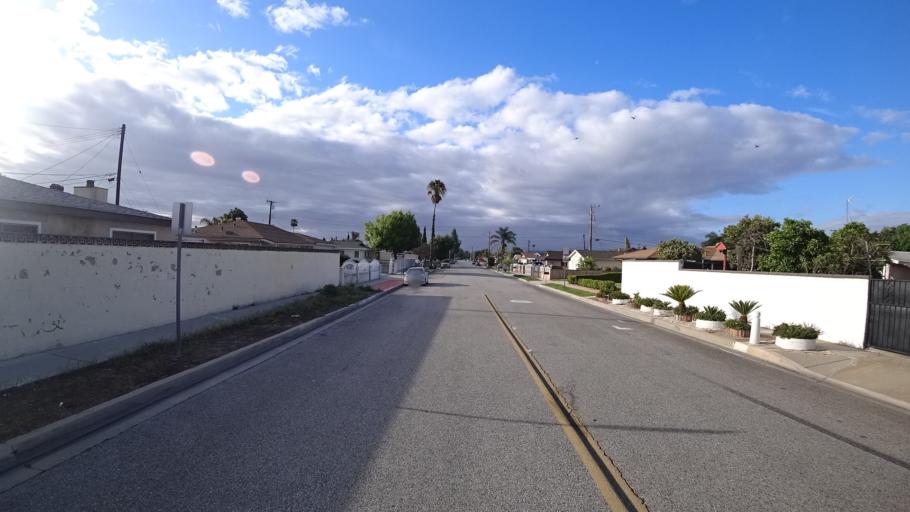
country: US
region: California
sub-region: Los Angeles County
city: Baldwin Park
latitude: 34.0973
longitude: -117.9725
